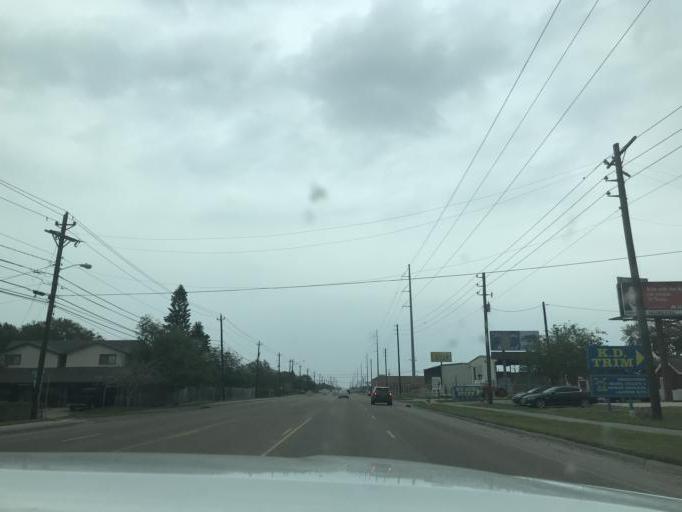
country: US
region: Texas
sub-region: Nueces County
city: Corpus Christi
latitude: 27.6960
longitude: -97.3713
